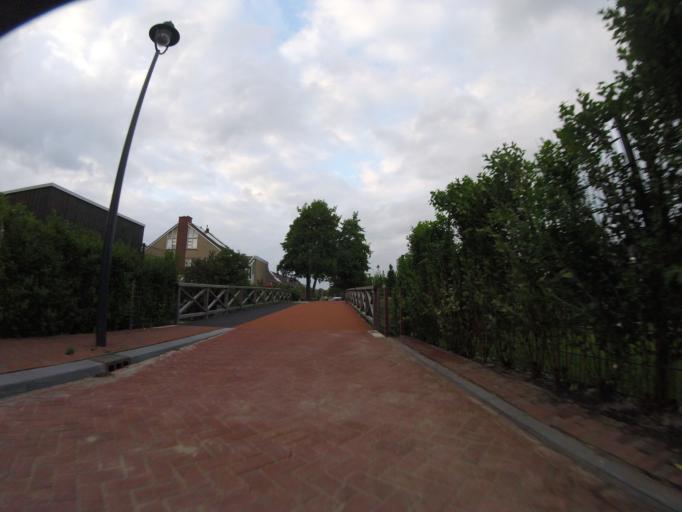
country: NL
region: North Holland
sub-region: Gemeente Haarlemmermeer
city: Hoofddorp
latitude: 52.2939
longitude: 4.6601
